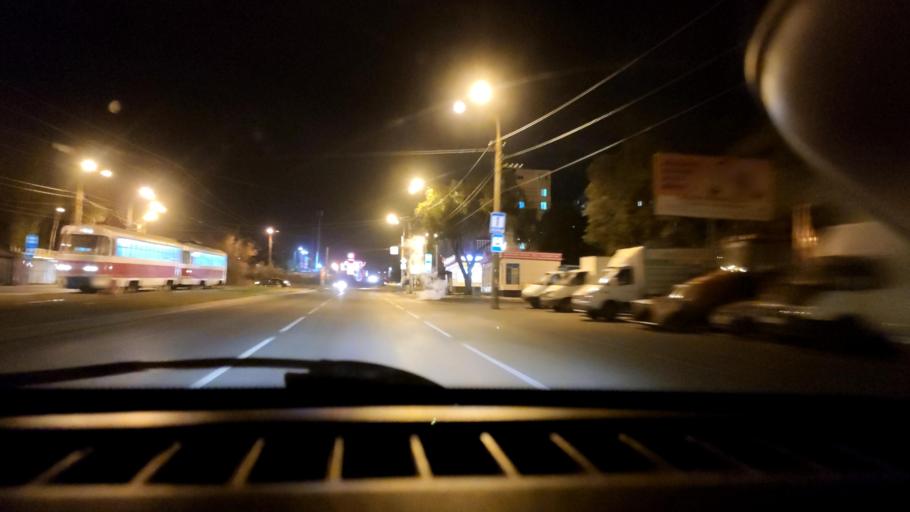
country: RU
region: Samara
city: Samara
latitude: 53.2162
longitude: 50.2232
